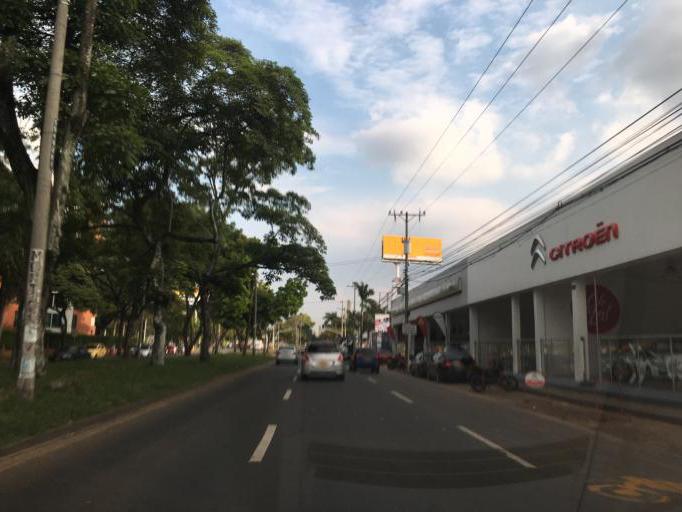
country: CO
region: Valle del Cauca
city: Cali
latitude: 3.3949
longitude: -76.5383
